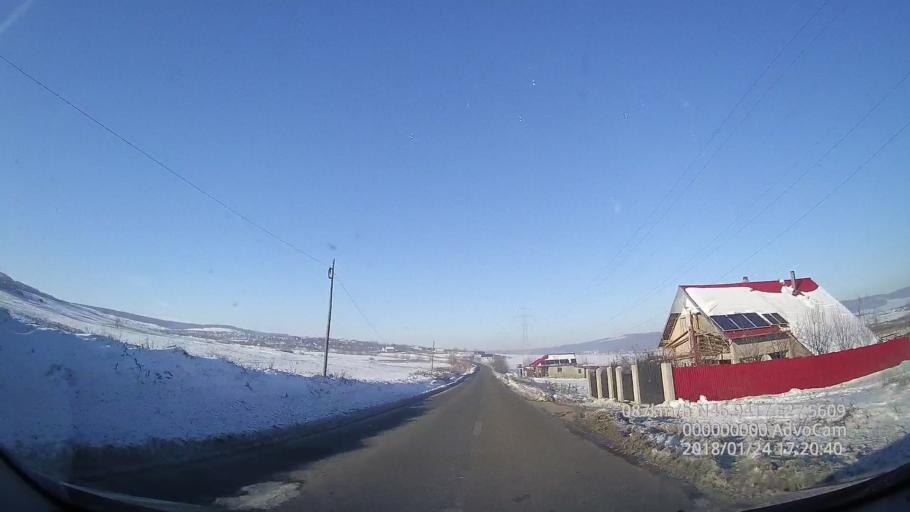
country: RO
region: Iasi
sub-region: Comuna Scanteia
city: Scanteia
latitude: 46.9425
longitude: 27.5607
